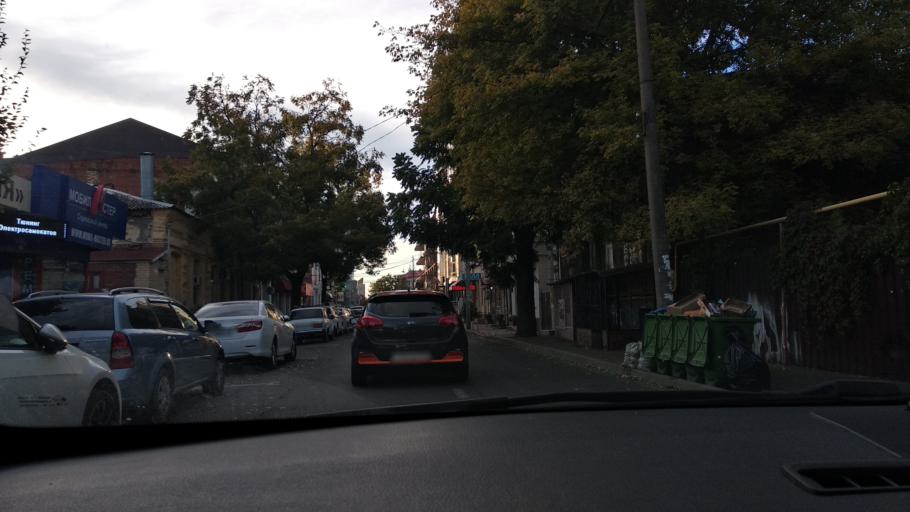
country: RU
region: Krasnodarskiy
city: Krasnodar
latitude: 45.0275
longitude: 38.9772
